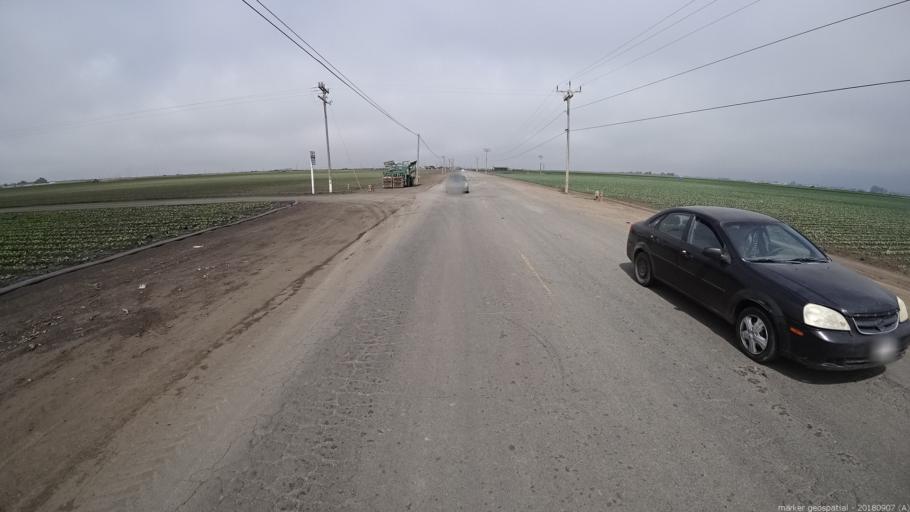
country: US
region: California
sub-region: Monterey County
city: Castroville
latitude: 36.7370
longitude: -121.7613
